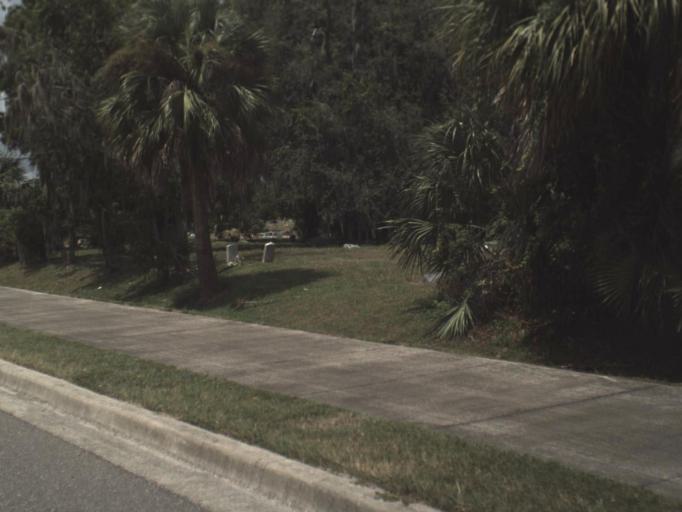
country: US
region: Florida
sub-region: Polk County
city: Bartow
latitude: 27.8965
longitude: -81.8550
